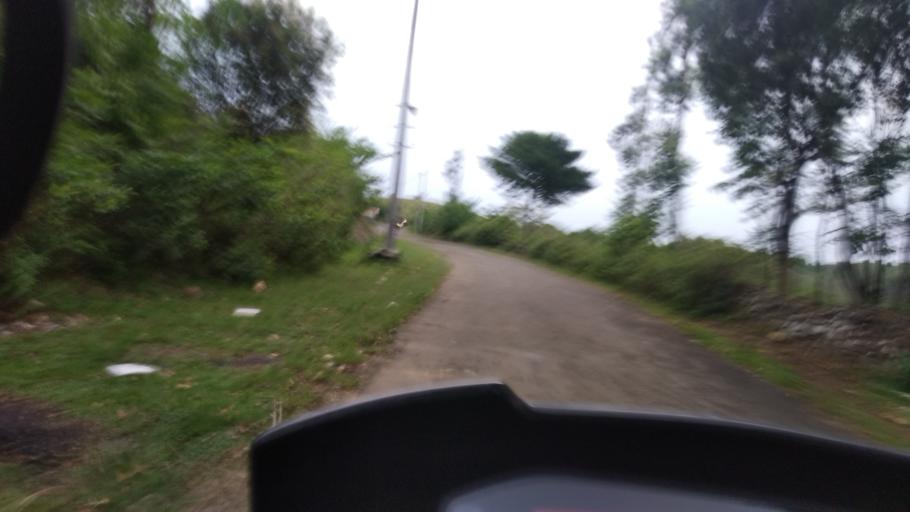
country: IN
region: Tamil Nadu
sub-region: Theni
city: Gudalur
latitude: 9.5482
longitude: 77.0345
